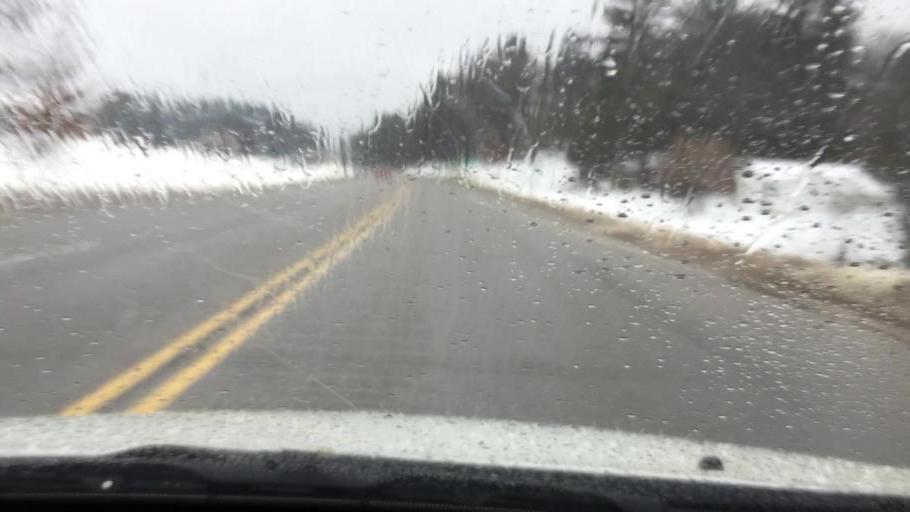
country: US
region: Michigan
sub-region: Wexford County
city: Manton
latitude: 44.5771
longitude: -85.3637
